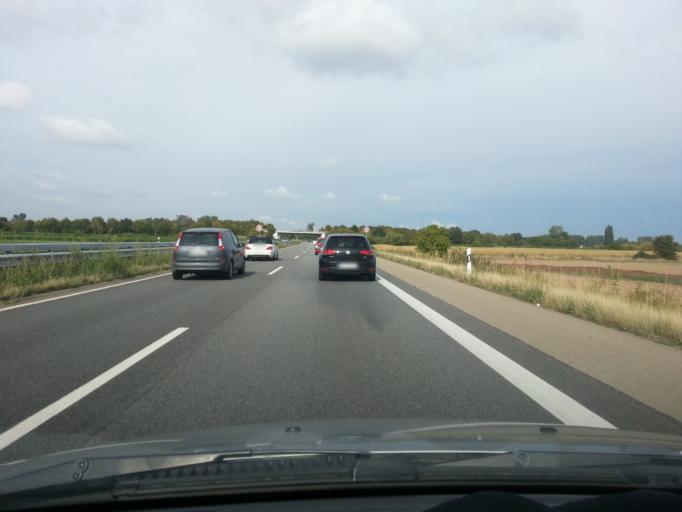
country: DE
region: Rheinland-Pfalz
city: Lachen-Speyerdorf
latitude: 49.3338
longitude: 8.1851
